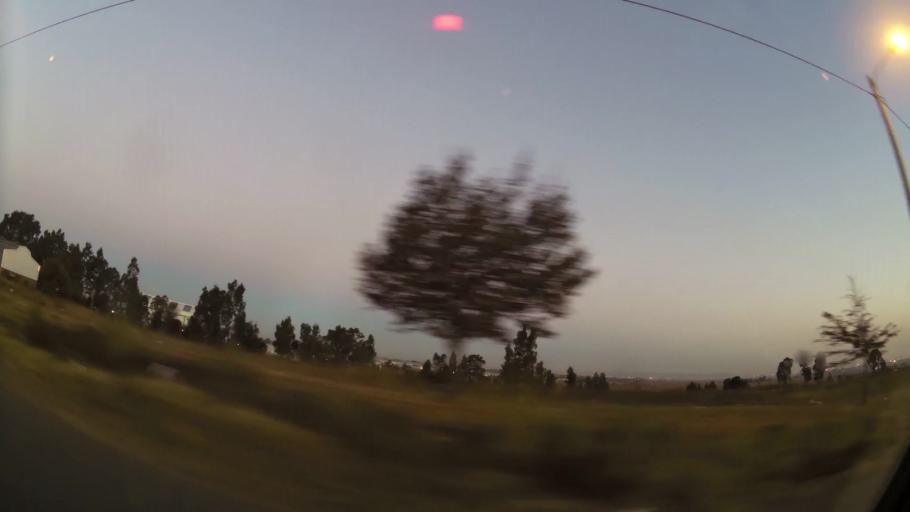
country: ZA
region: Gauteng
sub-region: Ekurhuleni Metropolitan Municipality
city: Germiston
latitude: -26.2809
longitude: 28.1701
